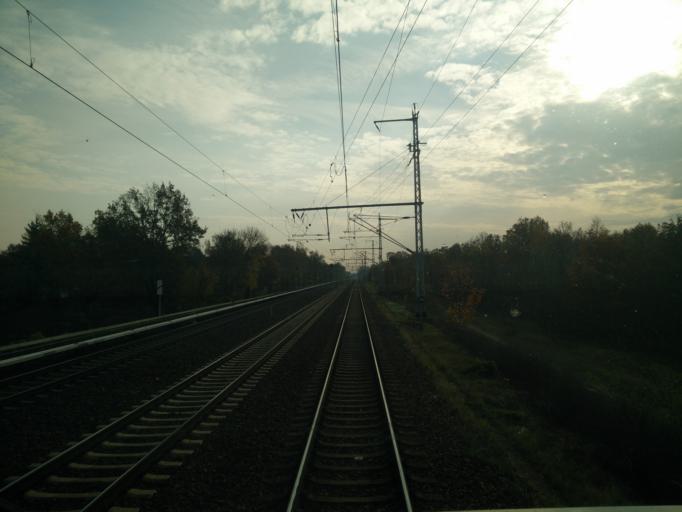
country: DE
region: Berlin
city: Karlshorst
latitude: 52.4745
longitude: 13.5405
